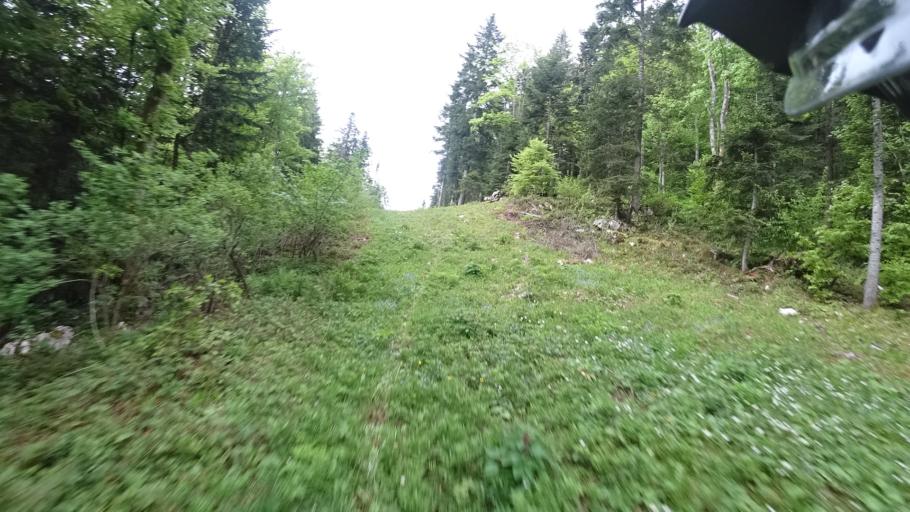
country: HR
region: Karlovacka
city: Plaski
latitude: 44.9639
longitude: 15.4054
